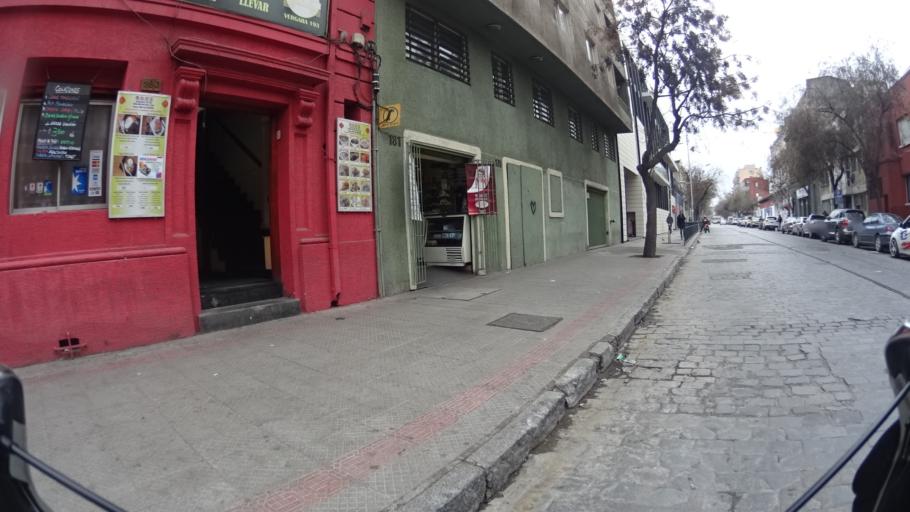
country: CL
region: Santiago Metropolitan
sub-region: Provincia de Santiago
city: Santiago
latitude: -33.4496
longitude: -70.6621
